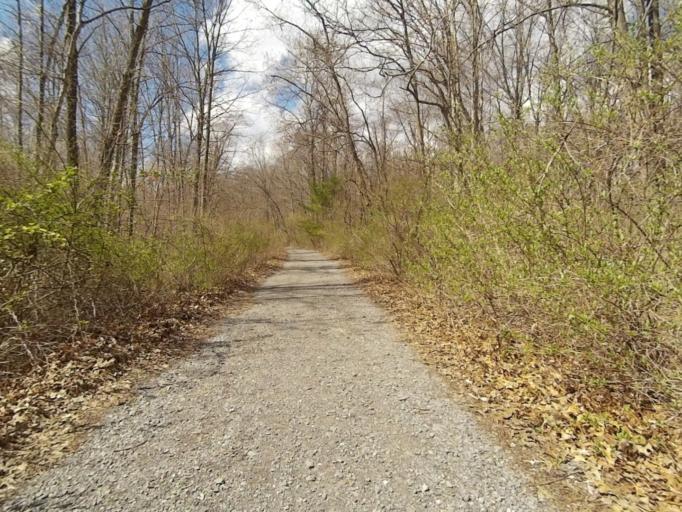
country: US
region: Pennsylvania
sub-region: Centre County
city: Park Forest Village
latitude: 40.8255
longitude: -77.9101
